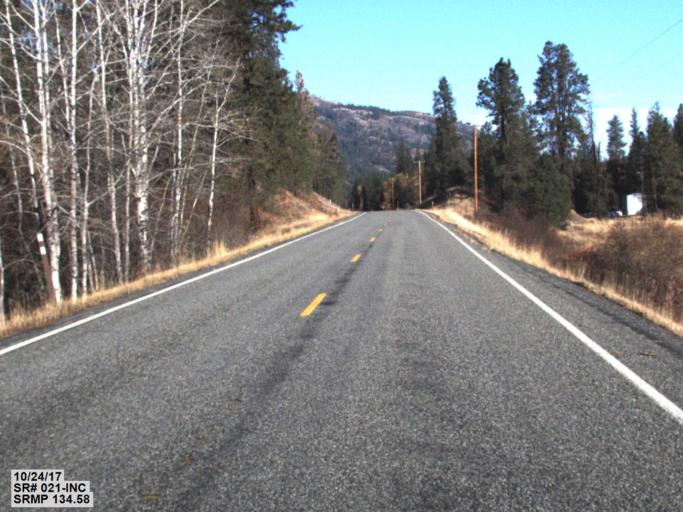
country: US
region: Washington
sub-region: Ferry County
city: Republic
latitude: 48.3147
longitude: -118.7398
